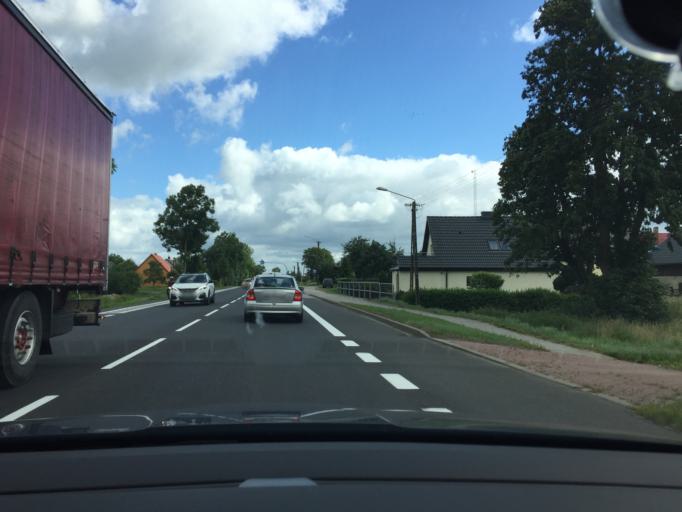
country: PL
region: West Pomeranian Voivodeship
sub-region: Powiat slawienski
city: Slawno
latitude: 54.3405
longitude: 16.6437
